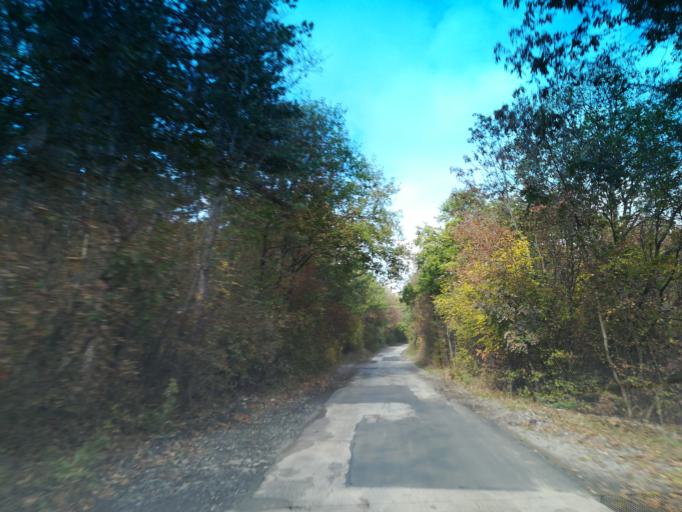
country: BG
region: Stara Zagora
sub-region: Obshtina Nikolaevo
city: Elkhovo
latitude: 42.3194
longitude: 25.4037
